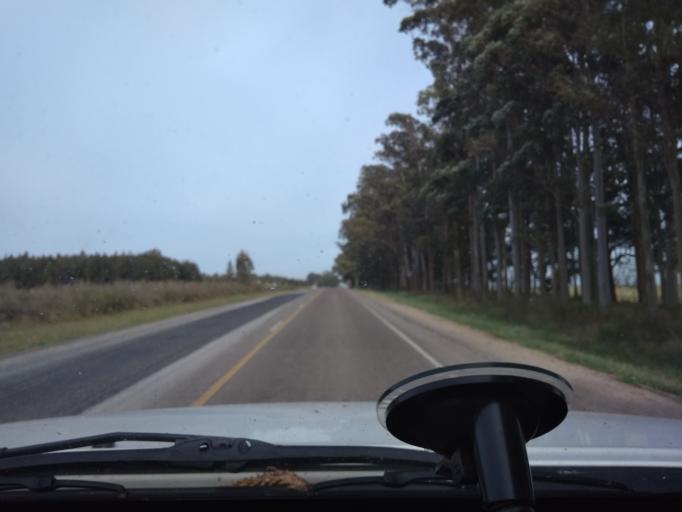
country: UY
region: Florida
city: Florida
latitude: -34.0641
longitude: -56.0499
